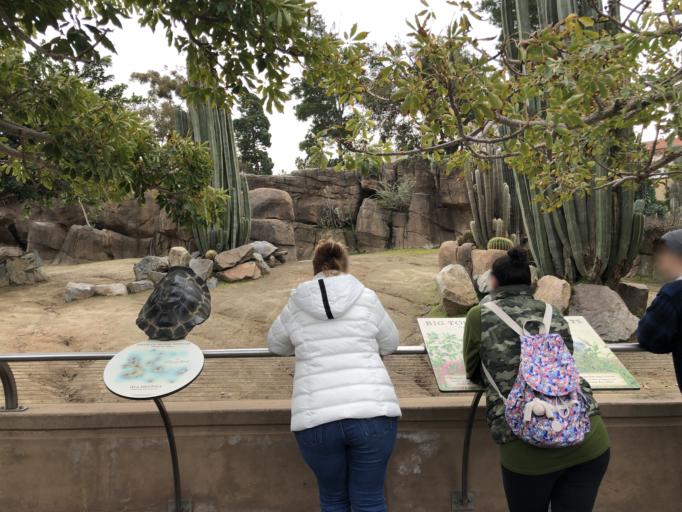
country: US
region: California
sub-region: San Diego County
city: San Diego
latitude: 32.7335
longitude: -117.1505
